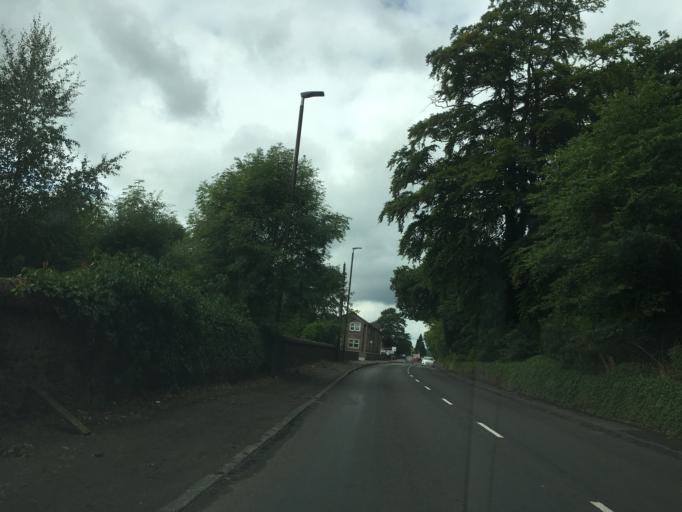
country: GB
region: Scotland
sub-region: Stirling
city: Stirling
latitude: 56.1346
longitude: -3.9146
